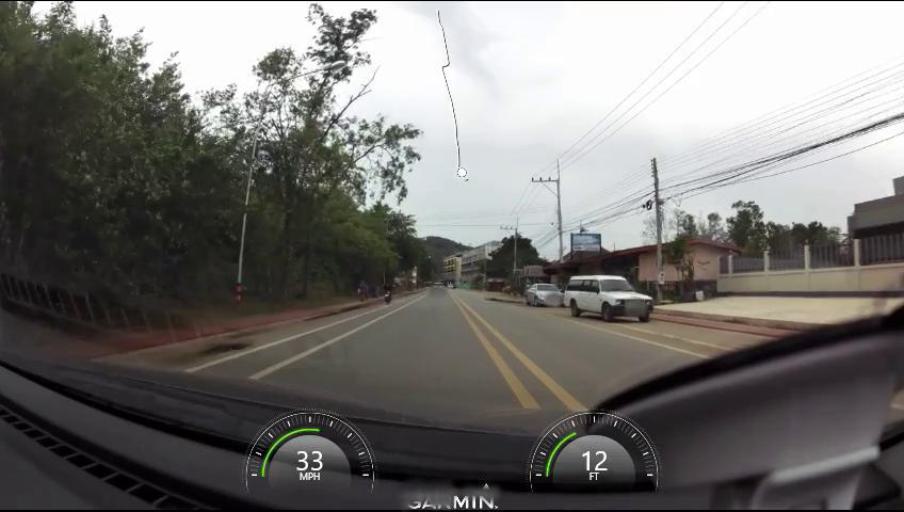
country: TH
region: Prachuap Khiri Khan
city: Pran Buri
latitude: 12.4633
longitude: 99.9743
